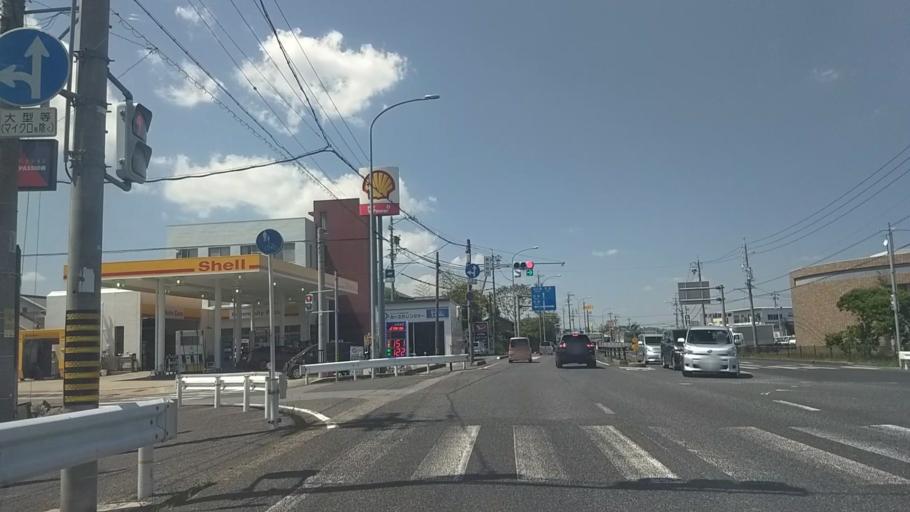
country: JP
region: Aichi
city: Okazaki
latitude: 34.9285
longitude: 137.1987
